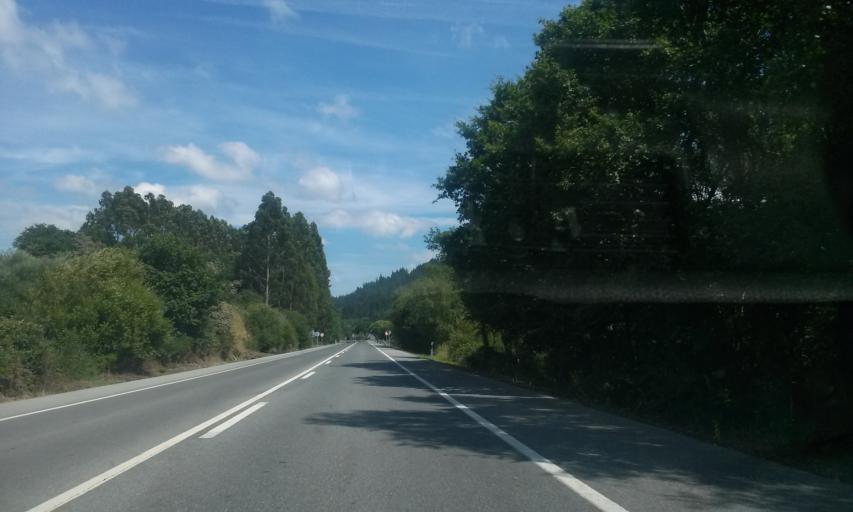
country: ES
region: Galicia
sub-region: Provincia de Lugo
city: Guitiriz
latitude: 43.1743
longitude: -7.8001
